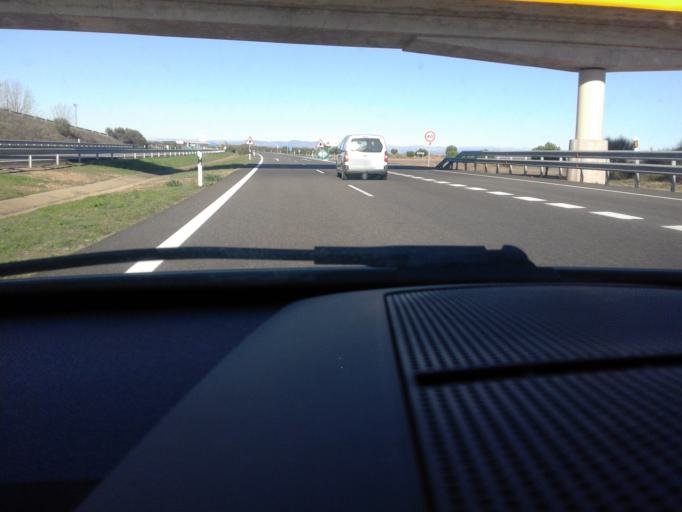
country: ES
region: Castille and Leon
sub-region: Provincia de Leon
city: Vega de Infanzones
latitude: 42.4846
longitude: -5.5535
